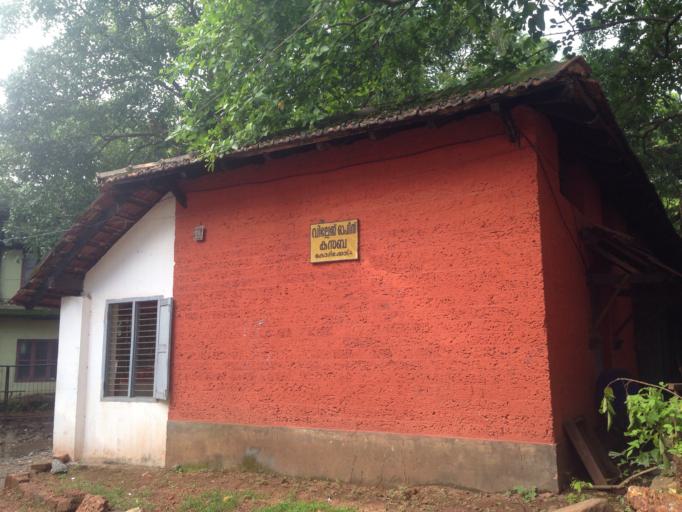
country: IN
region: Kerala
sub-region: Kozhikode
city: Kozhikode
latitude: 11.2532
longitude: 75.7909
